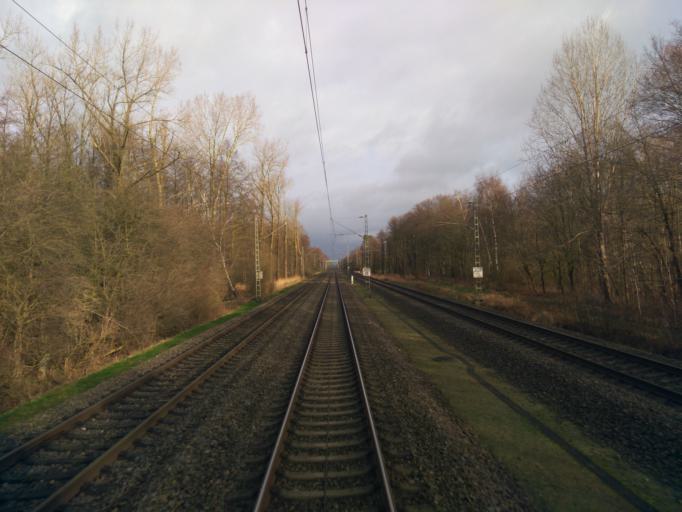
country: DE
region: Lower Saxony
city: Konigsmoor
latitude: 53.2461
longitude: 9.6758
